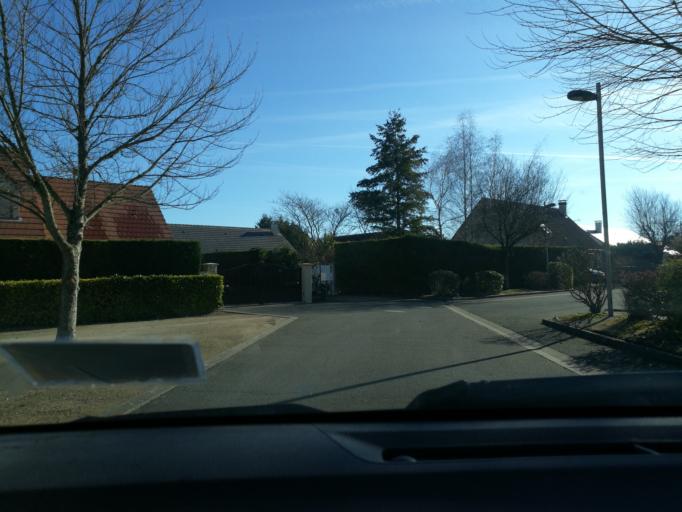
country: FR
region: Centre
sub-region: Departement du Loiret
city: Chaingy
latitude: 47.8836
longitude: 1.7785
